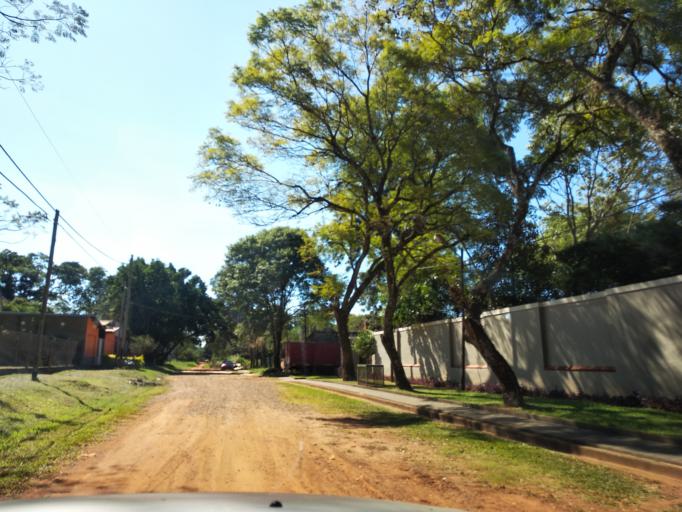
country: AR
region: Misiones
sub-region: Departamento de Capital
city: Posadas
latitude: -27.4318
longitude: -55.8865
